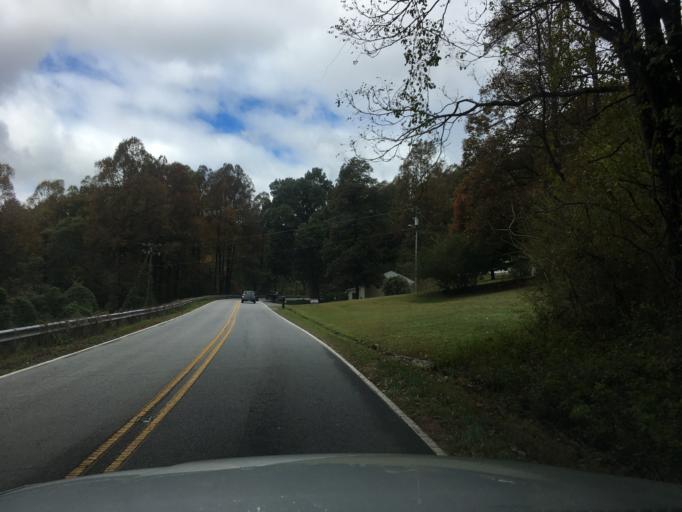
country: US
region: North Carolina
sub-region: Henderson County
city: Flat Rock
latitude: 35.2456
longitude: -82.4210
